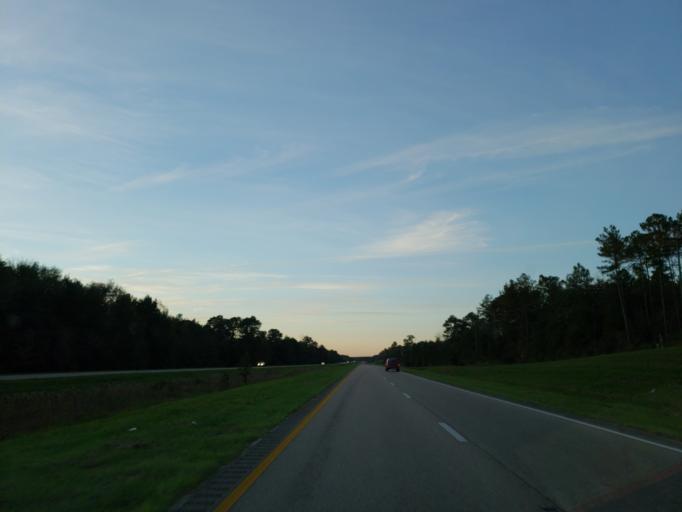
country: US
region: Mississippi
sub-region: Wayne County
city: Belmont
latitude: 31.5826
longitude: -88.5432
